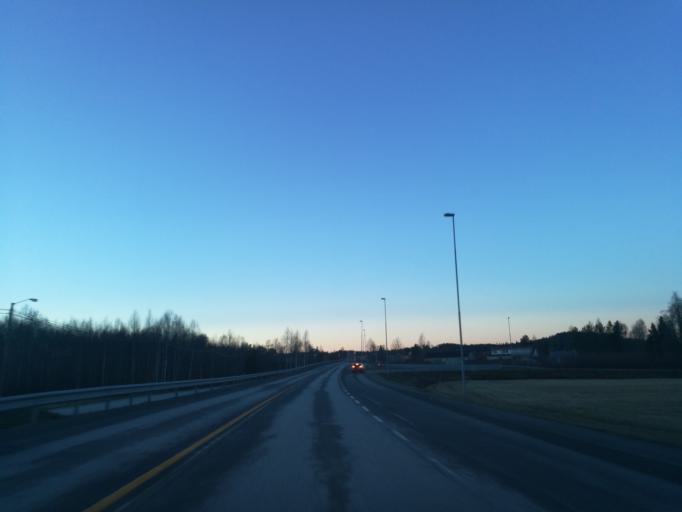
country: NO
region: Hedmark
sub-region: Eidskog
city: Skotterud
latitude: 59.9789
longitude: 12.1182
